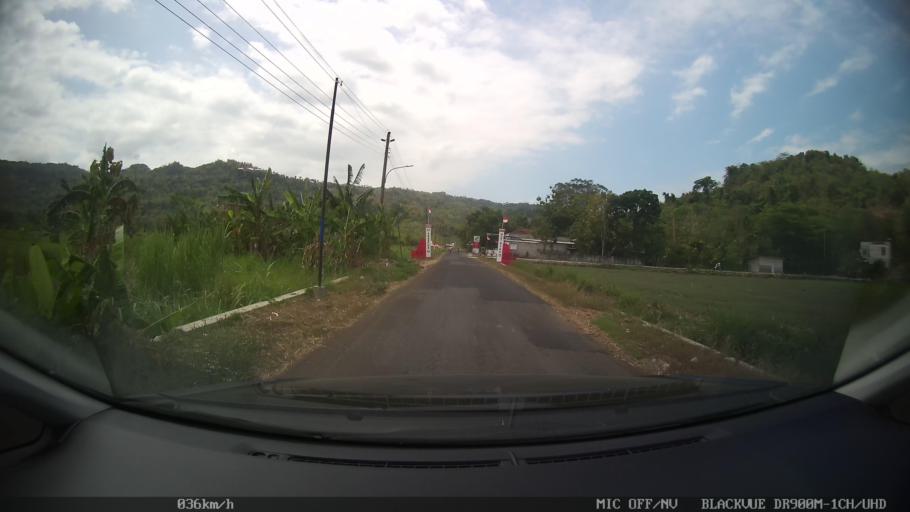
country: ID
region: Central Java
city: Candi Prambanan
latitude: -7.8113
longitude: 110.5065
